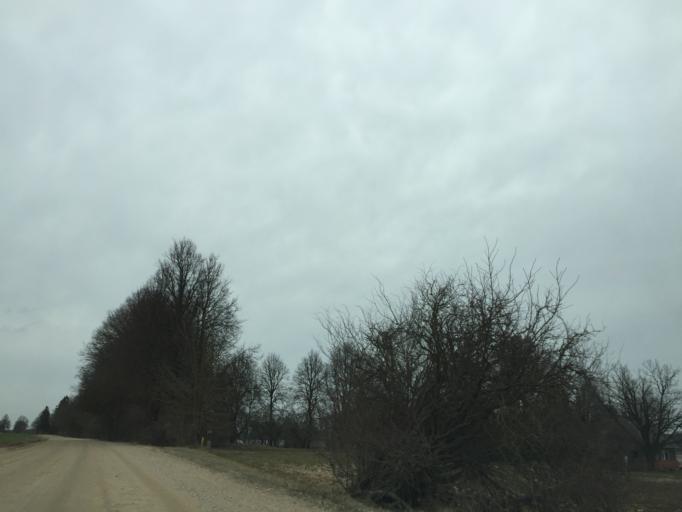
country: LV
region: Livani
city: Livani
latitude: 56.2900
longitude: 26.1763
